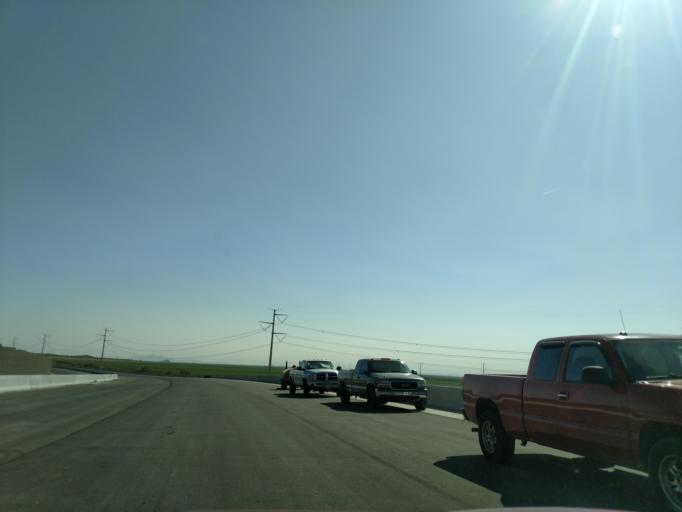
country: US
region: Arizona
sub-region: Maricopa County
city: Laveen
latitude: 33.2914
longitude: -112.1318
